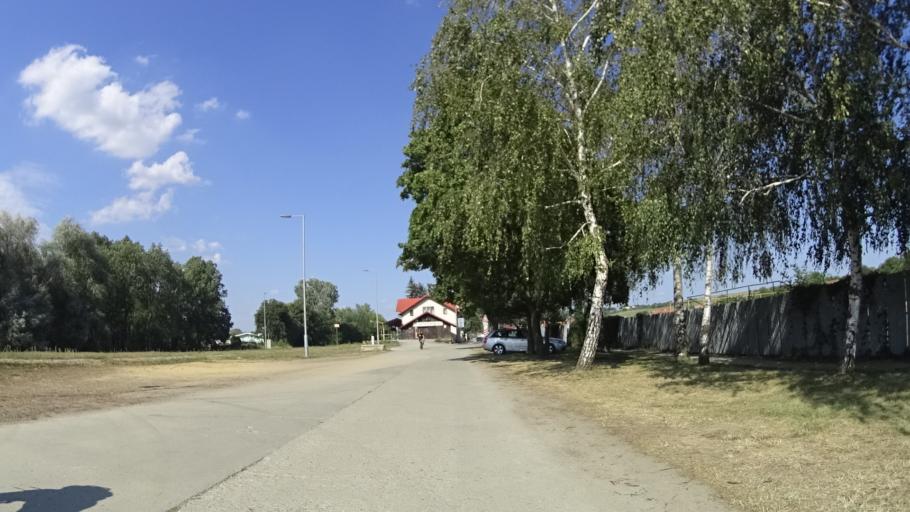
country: CZ
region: Zlin
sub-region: Okres Zlin
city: Ostrozska Nova Ves
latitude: 49.0089
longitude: 17.4360
